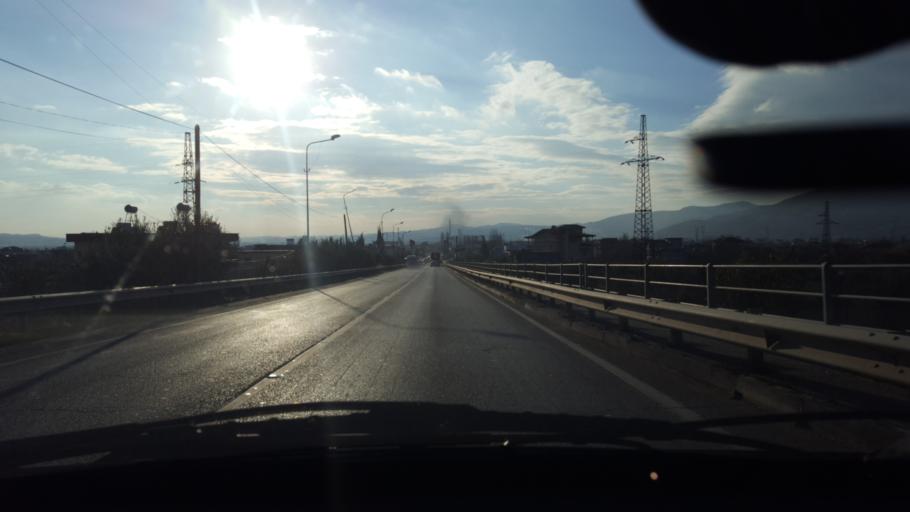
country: AL
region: Elbasan
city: Elbasan
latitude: 41.1050
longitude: 20.0618
